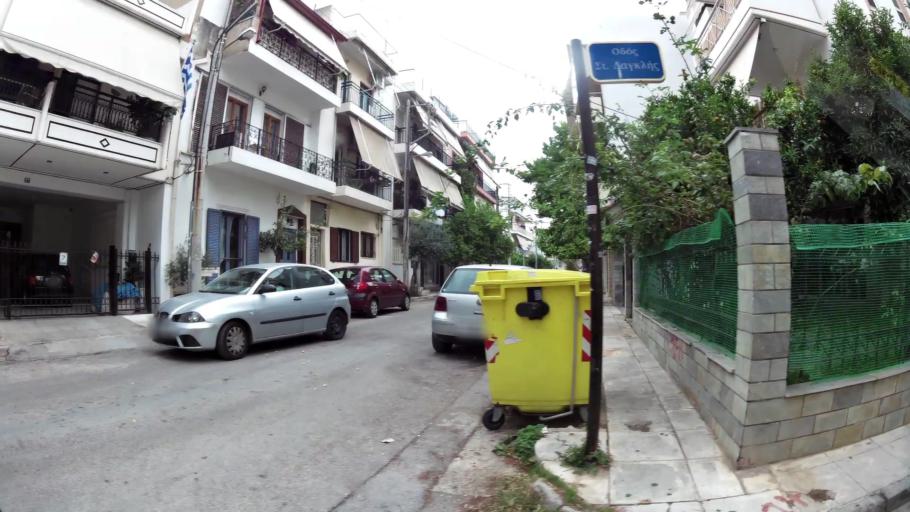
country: GR
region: Attica
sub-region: Nomarchia Athinas
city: Chaidari
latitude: 38.0016
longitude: 23.6786
